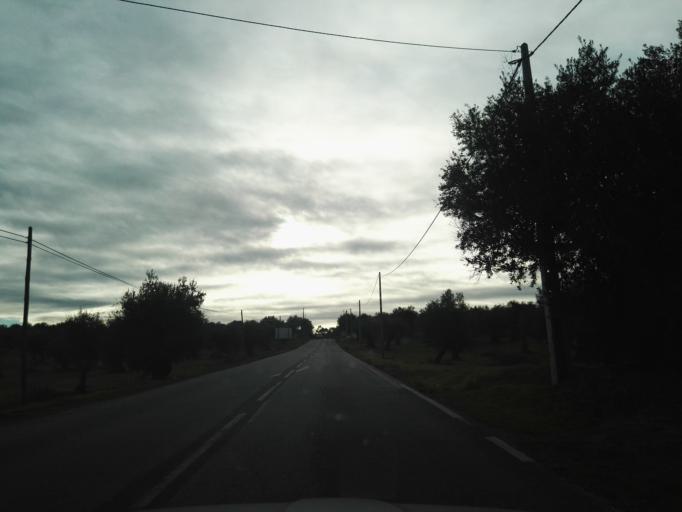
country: PT
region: Evora
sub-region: Redondo
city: Redondo
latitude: 38.6557
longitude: -7.5364
